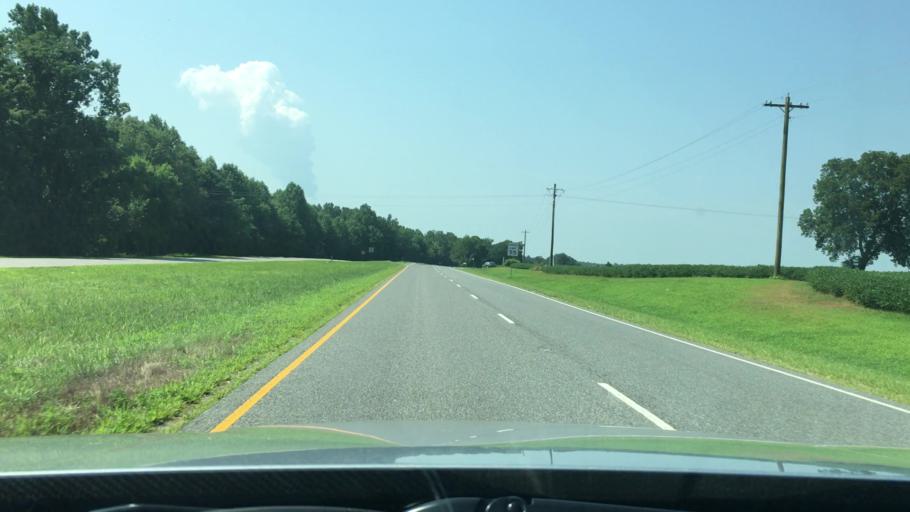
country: US
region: Virginia
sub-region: Caroline County
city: Bowling Green
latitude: 37.9872
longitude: -77.4186
